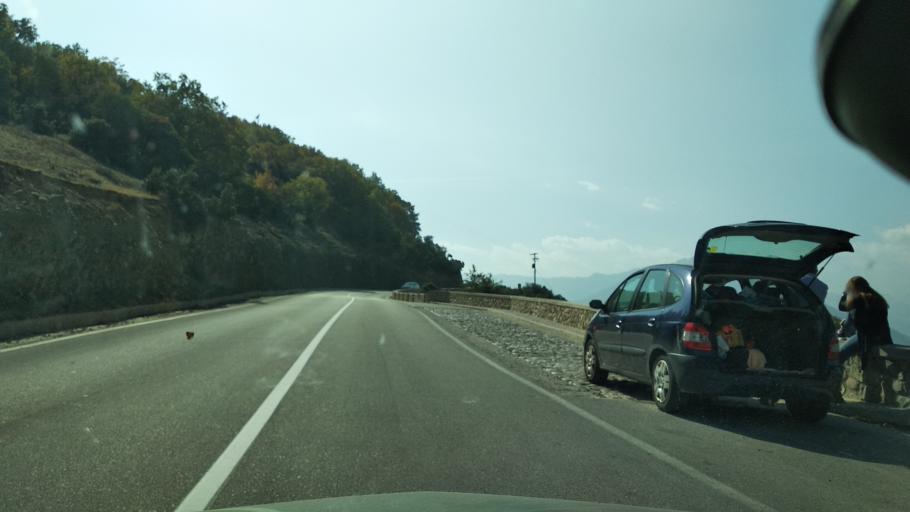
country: GR
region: Thessaly
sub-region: Trikala
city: Kalampaka
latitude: 39.7152
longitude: 21.6398
